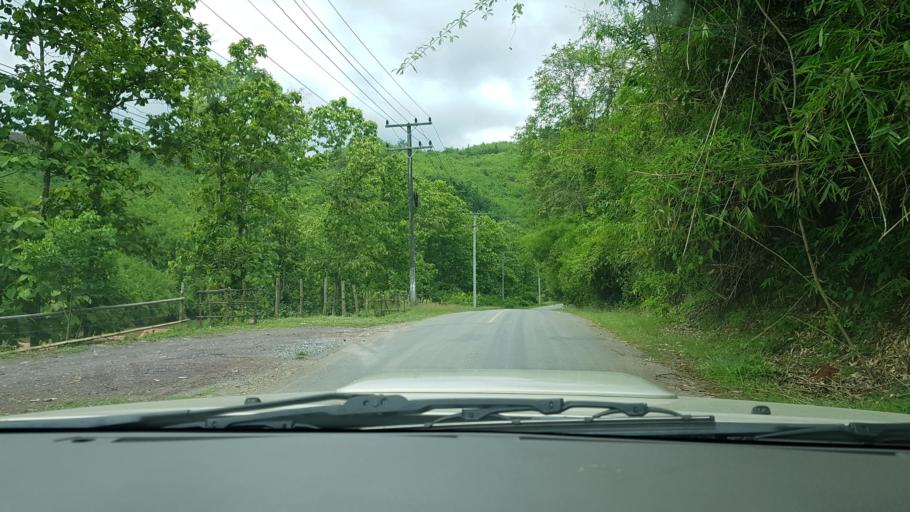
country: TH
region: Nan
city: Chaloem Phra Kiat
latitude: 19.9500
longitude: 101.2516
